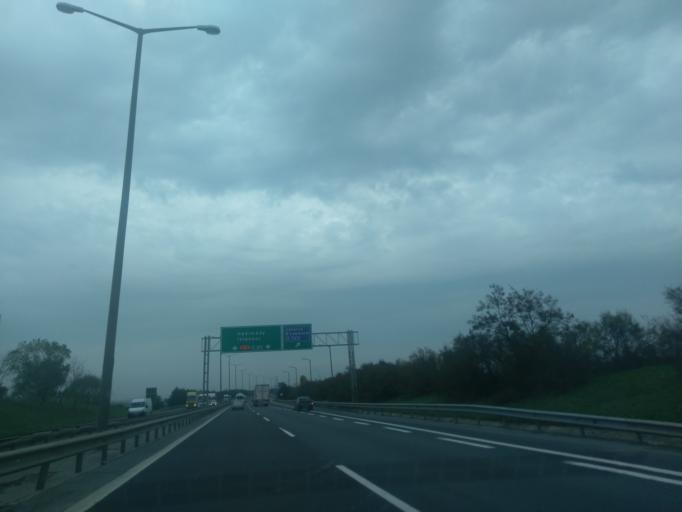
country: TR
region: Istanbul
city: Muratbey
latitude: 41.0836
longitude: 28.5080
